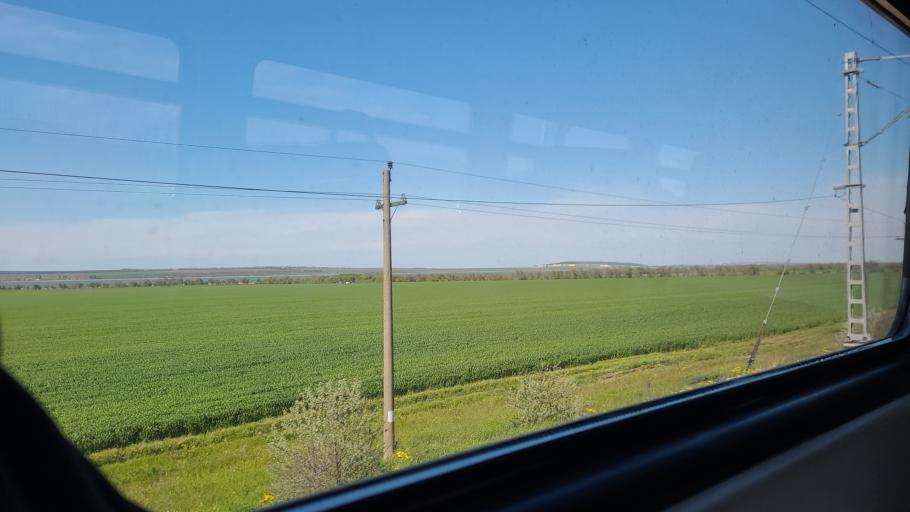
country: RU
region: Krasnodarskiy
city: Starotitarovskaya
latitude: 45.1983
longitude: 37.2072
